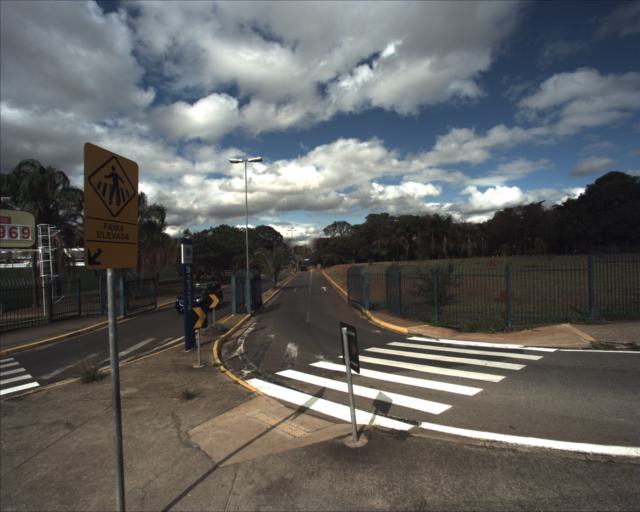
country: BR
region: Sao Paulo
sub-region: Sorocaba
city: Sorocaba
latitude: -23.4867
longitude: -47.4727
